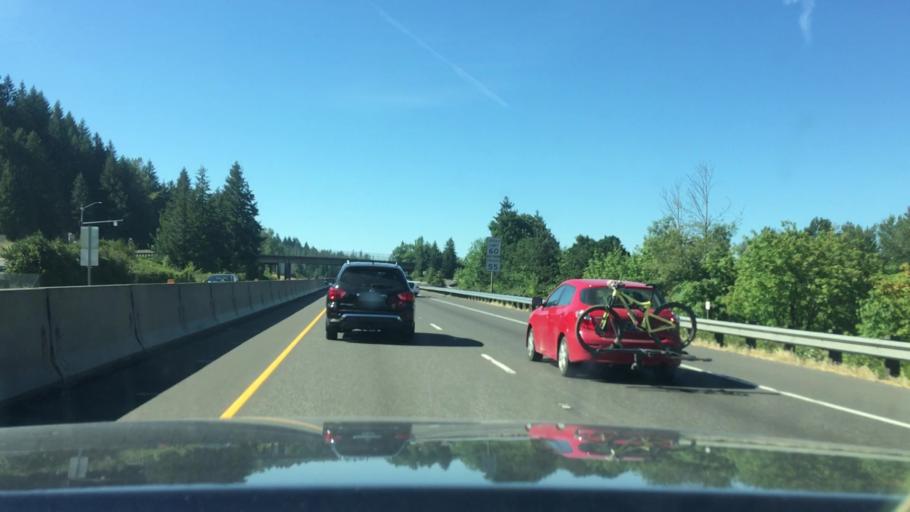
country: US
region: Oregon
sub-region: Lane County
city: Springfield
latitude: 44.0199
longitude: -123.0261
